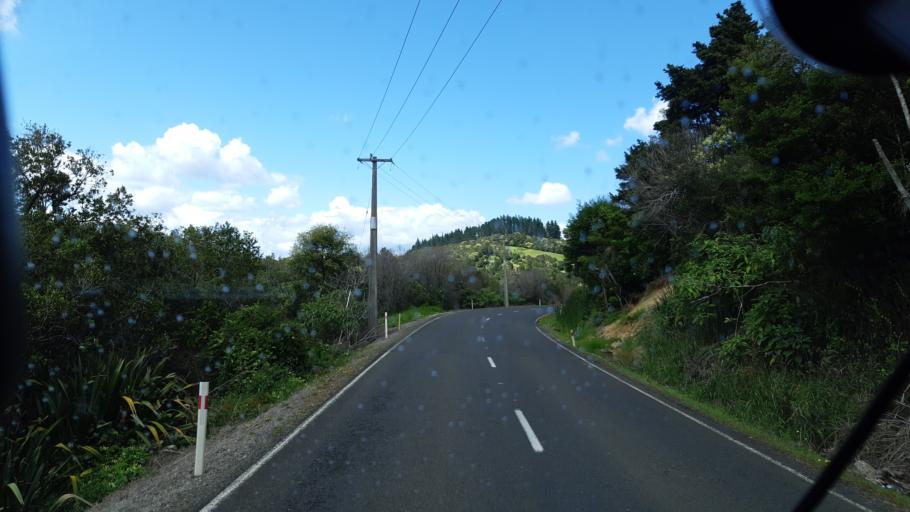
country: NZ
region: Northland
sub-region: Far North District
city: Taipa
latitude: -35.2706
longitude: 173.5228
